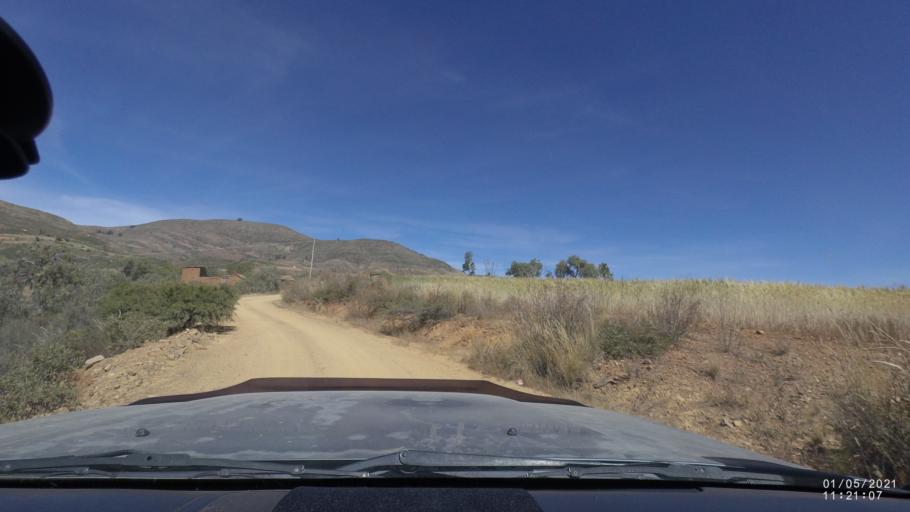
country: BO
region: Cochabamba
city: Tarata
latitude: -17.6445
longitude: -66.1255
